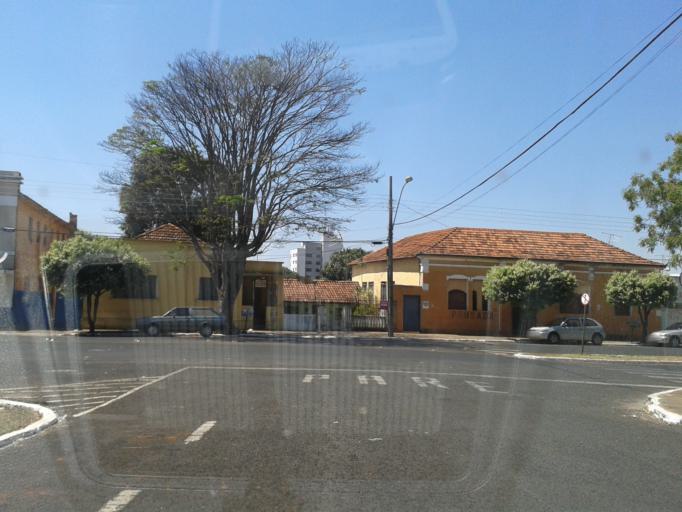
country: BR
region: Minas Gerais
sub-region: Araguari
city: Araguari
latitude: -18.6448
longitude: -48.1971
